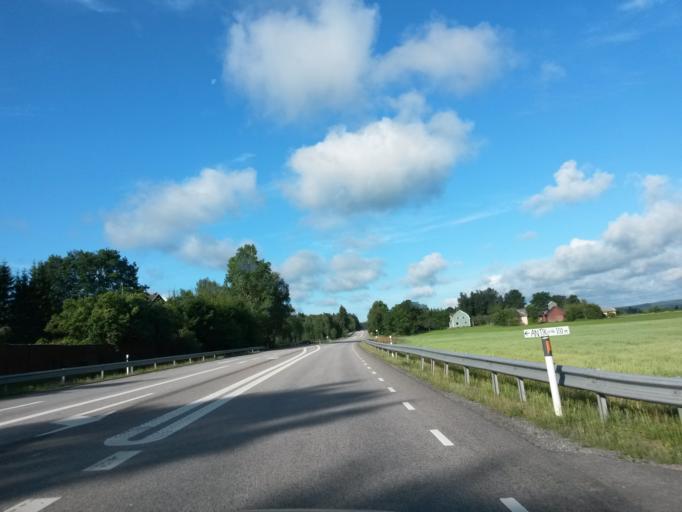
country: SE
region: Vaestra Goetaland
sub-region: Vargarda Kommun
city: Jonstorp
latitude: 57.9969
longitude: 12.7174
